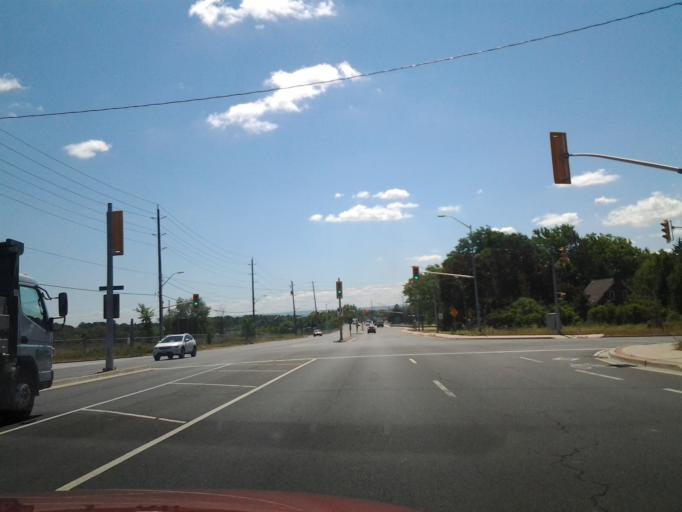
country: CA
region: Ontario
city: Hamilton
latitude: 43.3138
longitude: -79.8625
